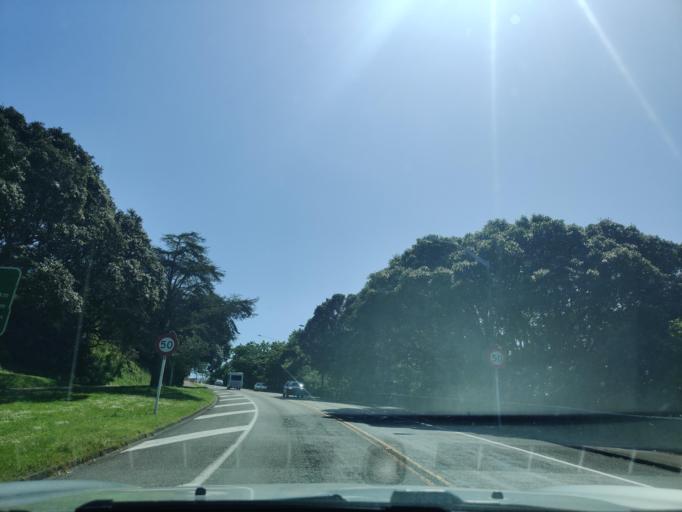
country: NZ
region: Manawatu-Wanganui
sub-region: Wanganui District
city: Wanganui
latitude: -39.9214
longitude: 175.0387
